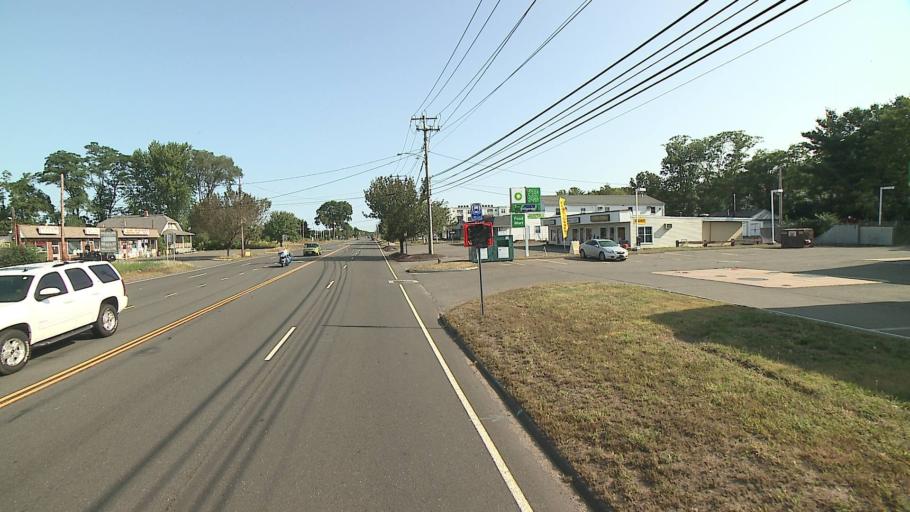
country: US
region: Connecticut
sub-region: New Haven County
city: North Haven
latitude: 41.4146
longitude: -72.8411
